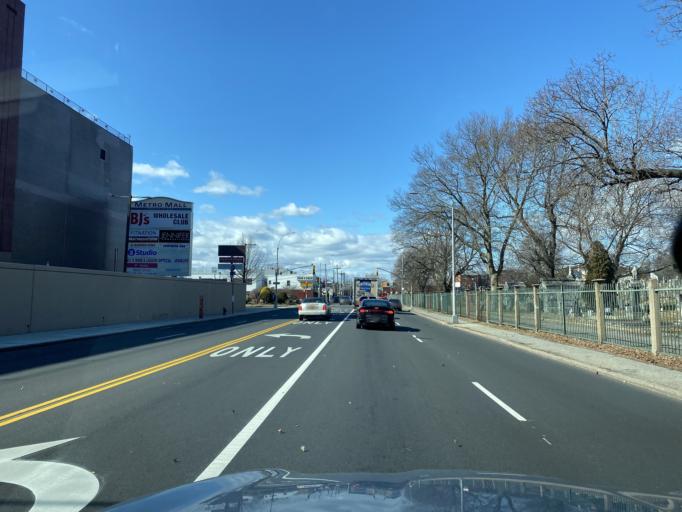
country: US
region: New York
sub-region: Kings County
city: East New York
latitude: 40.7125
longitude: -73.8927
